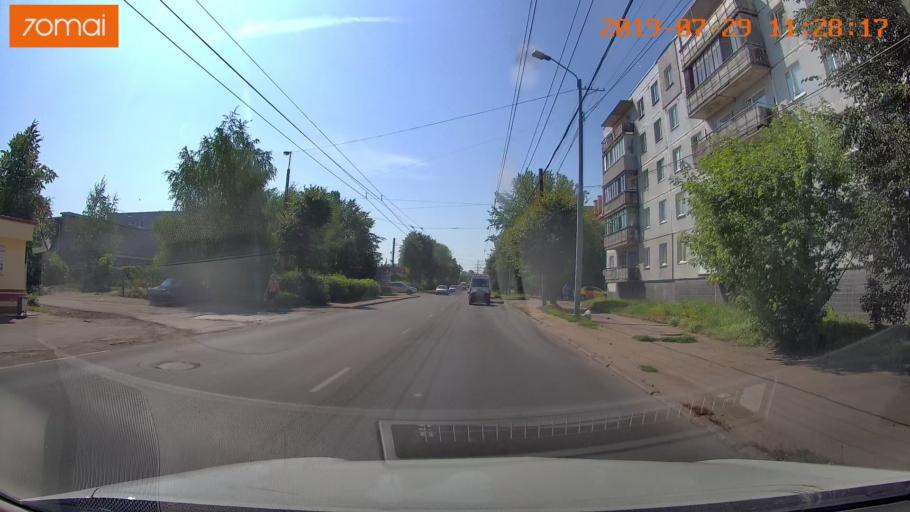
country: RU
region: Kaliningrad
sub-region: Gorod Kaliningrad
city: Kaliningrad
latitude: 54.6876
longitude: 20.5326
